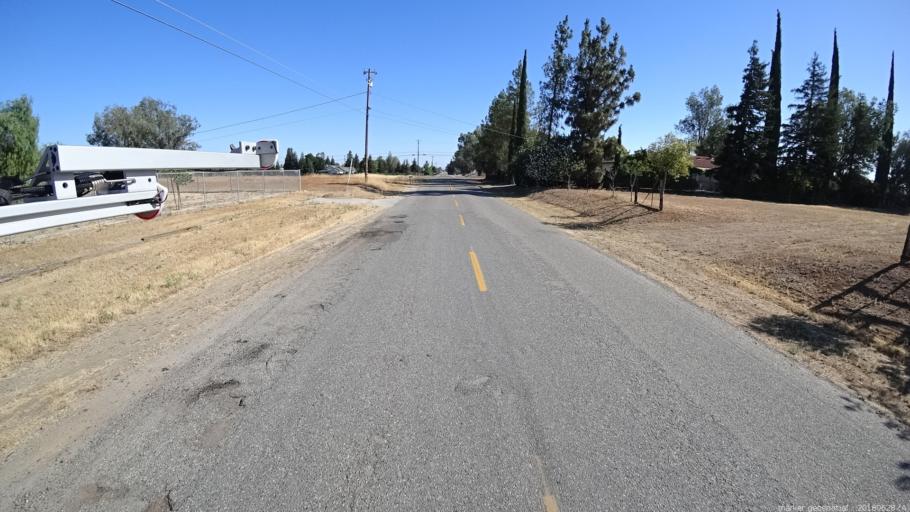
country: US
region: California
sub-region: Madera County
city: Bonadelle Ranchos-Madera Ranchos
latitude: 36.9876
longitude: -119.8866
